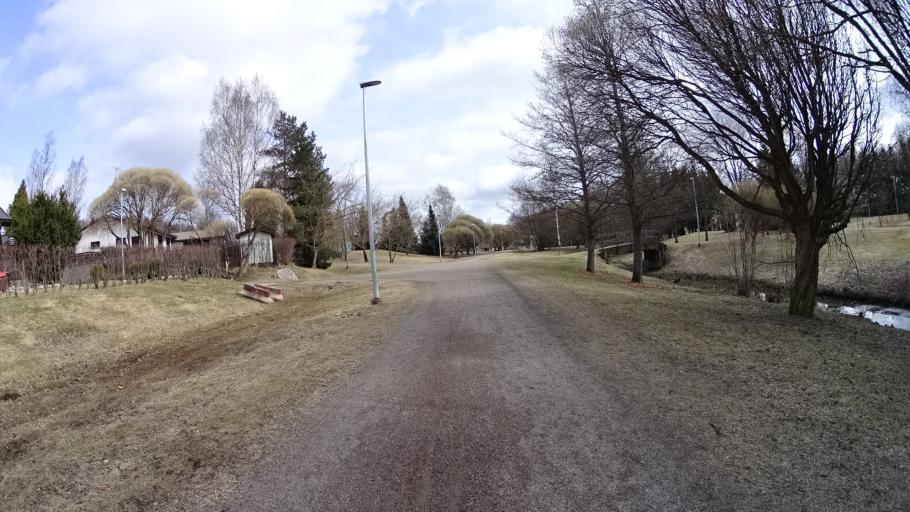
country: FI
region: Uusimaa
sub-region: Helsinki
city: Kilo
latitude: 60.2683
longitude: 24.7984
